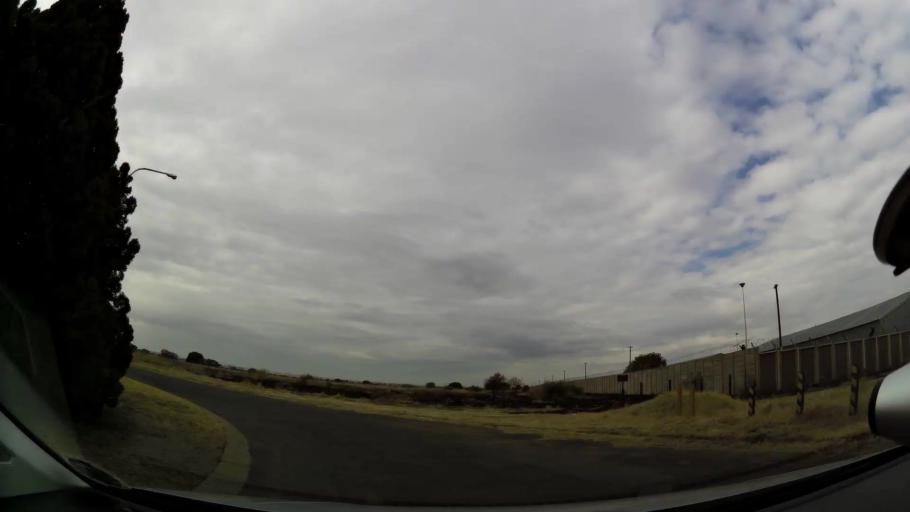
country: ZA
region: Orange Free State
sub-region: Fezile Dabi District Municipality
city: Kroonstad
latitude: -27.6358
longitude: 27.2425
